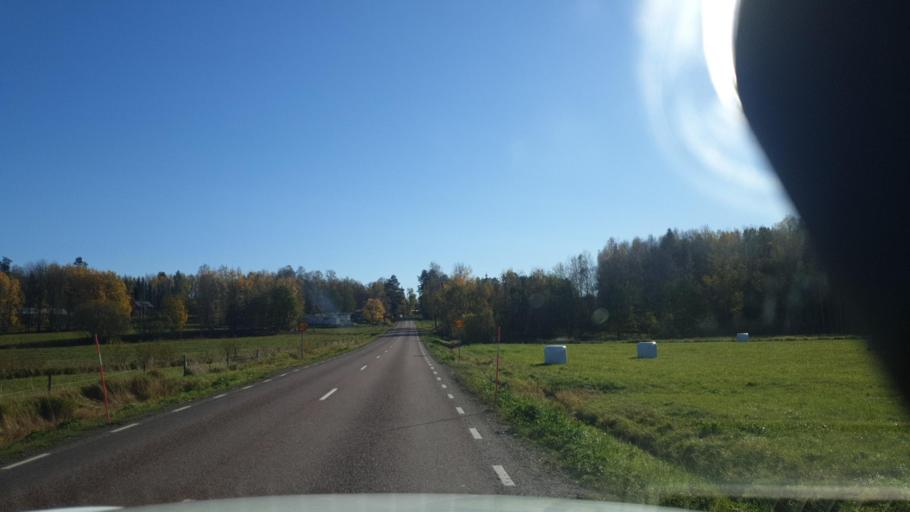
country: SE
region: Vaermland
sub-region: Grums Kommun
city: Grums
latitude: 59.4532
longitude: 12.9695
